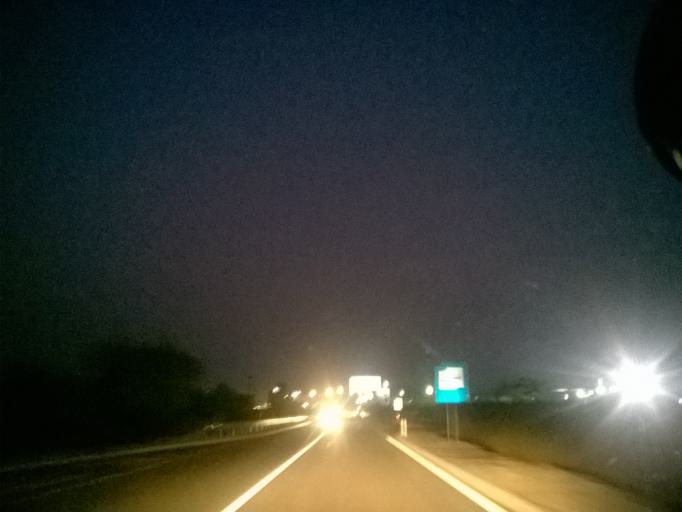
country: ME
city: Mojanovici
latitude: 42.3965
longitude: 19.1569
